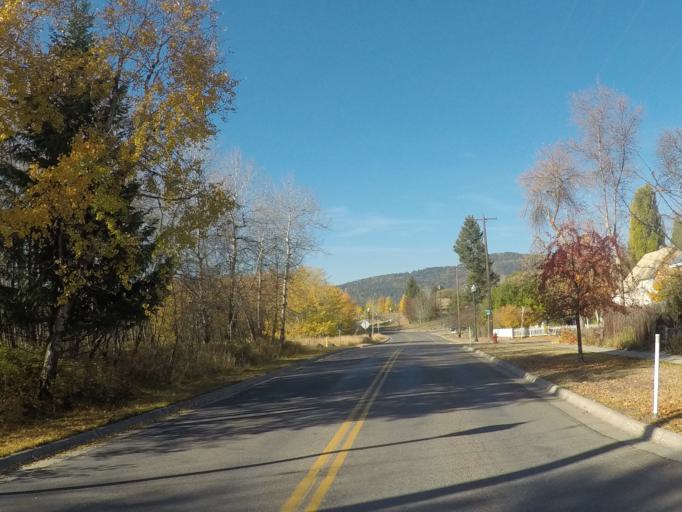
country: US
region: Montana
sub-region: Flathead County
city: Whitefish
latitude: 48.4152
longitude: -114.3459
